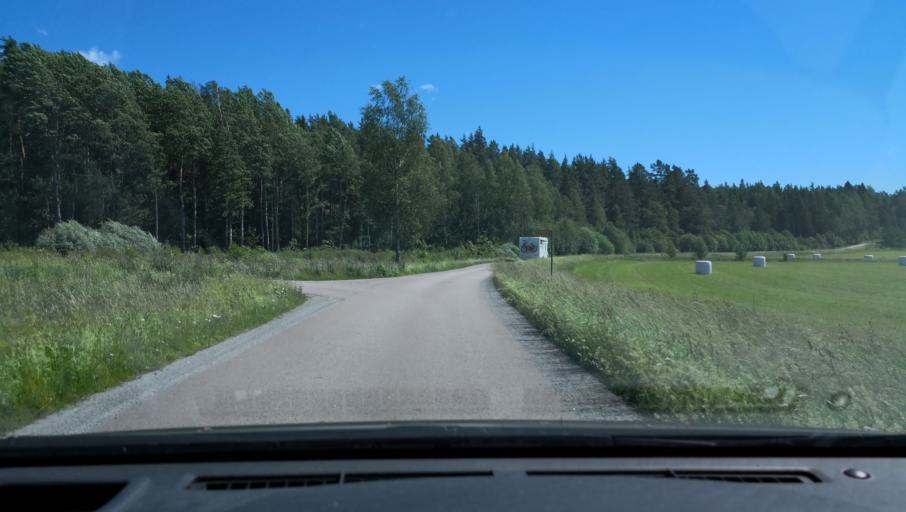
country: SE
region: Vaestmanland
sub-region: Arboga Kommun
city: Tyringe
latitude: 59.3926
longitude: 15.9420
